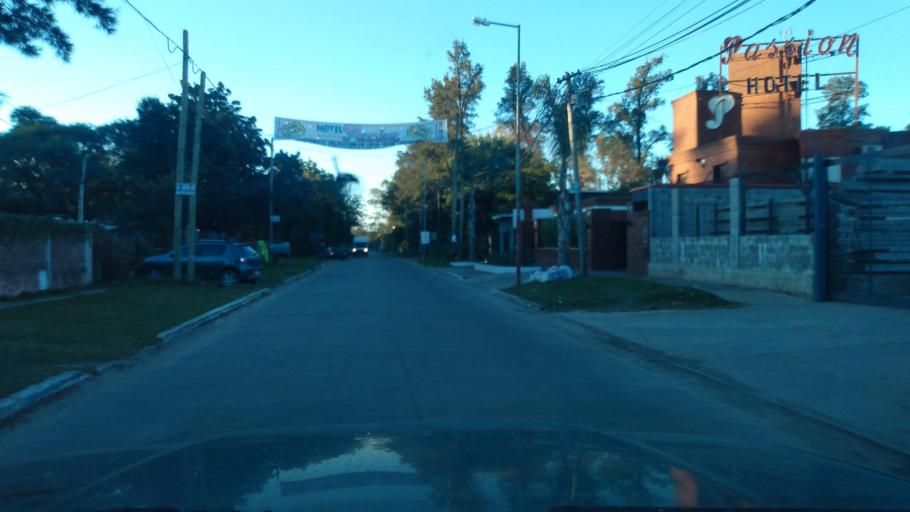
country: AR
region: Buenos Aires
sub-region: Partido de Merlo
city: Merlo
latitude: -34.6601
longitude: -58.7498
